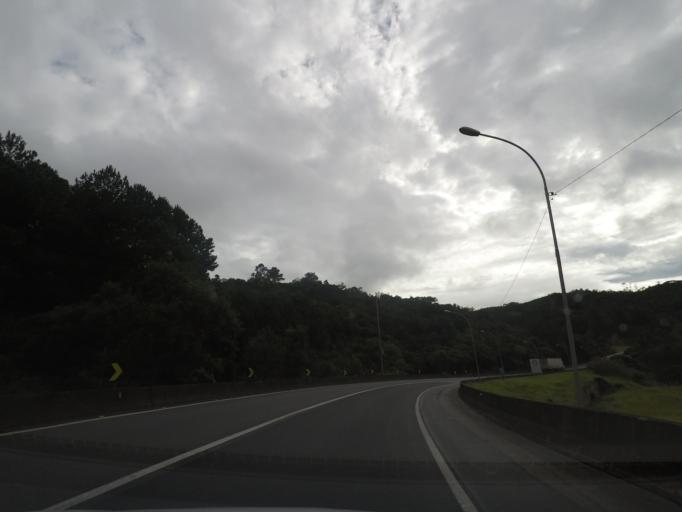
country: BR
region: Parana
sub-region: Campina Grande Do Sul
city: Campina Grande do Sul
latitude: -25.1125
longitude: -48.8472
